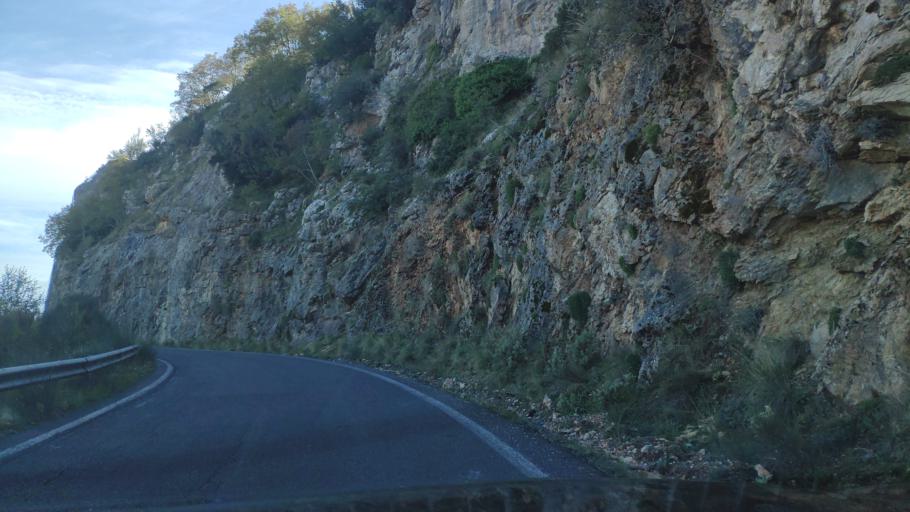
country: GR
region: Peloponnese
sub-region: Nomos Arkadias
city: Dimitsana
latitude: 37.5937
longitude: 22.0308
